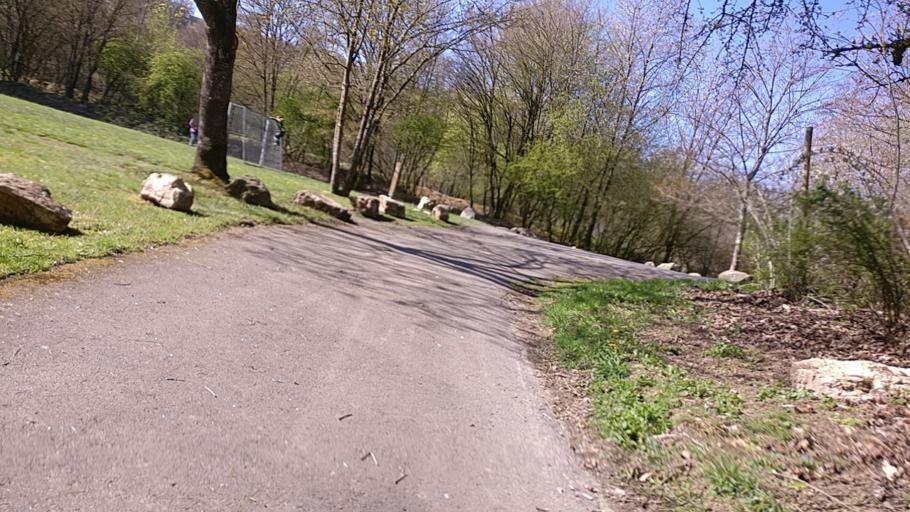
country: DE
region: Rheinland-Pfalz
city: Peterslahr
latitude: 50.6254
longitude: 7.4366
